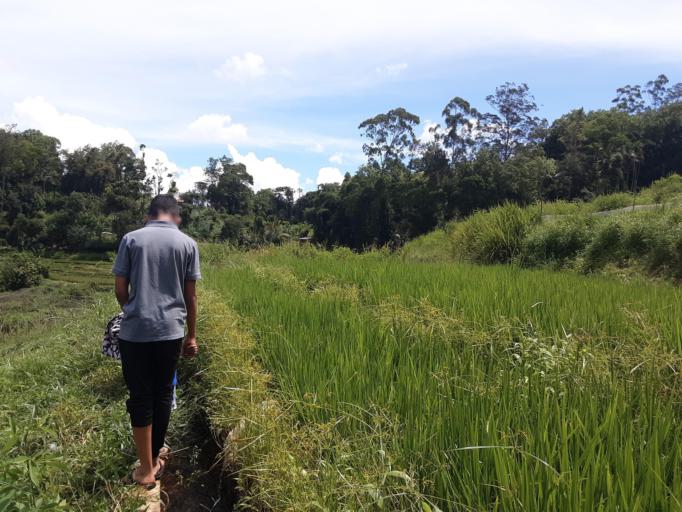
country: LK
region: Uva
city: Haputale
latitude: 6.8955
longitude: 80.9259
